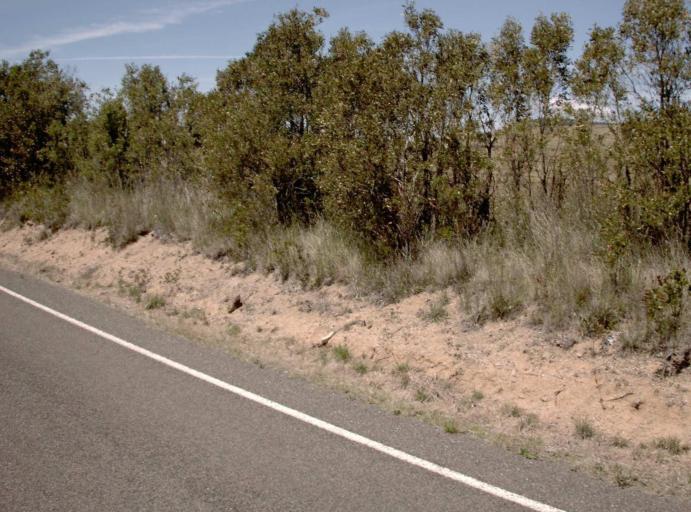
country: AU
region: Victoria
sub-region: Alpine
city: Mount Beauty
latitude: -37.1510
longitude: 147.6503
